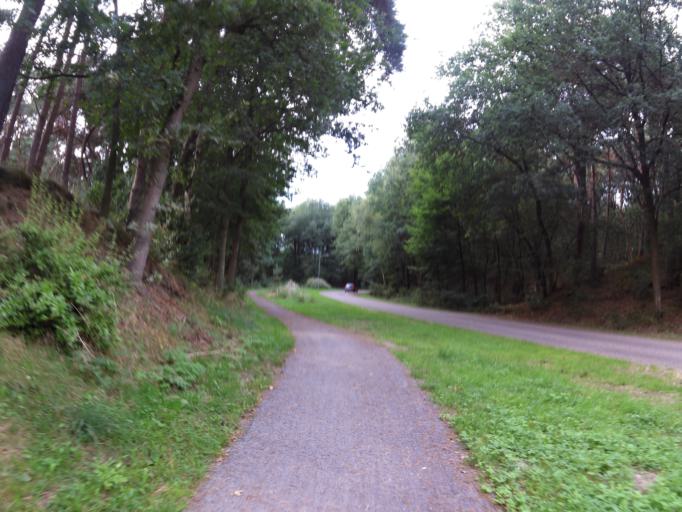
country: NL
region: Drenthe
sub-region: Gemeente Westerveld
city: Dwingeloo
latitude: 52.8189
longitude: 6.3703
